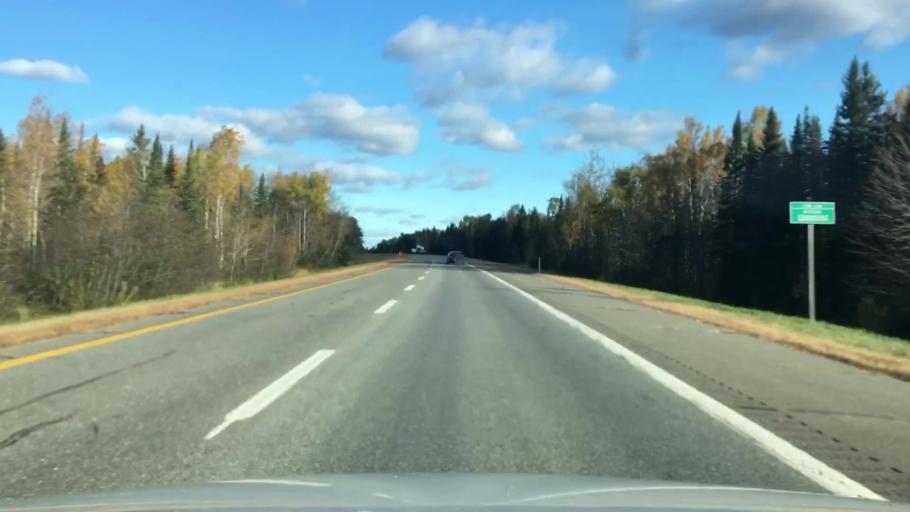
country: US
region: Maine
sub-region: Penobscot County
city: Greenbush
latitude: 45.1206
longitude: -68.6939
